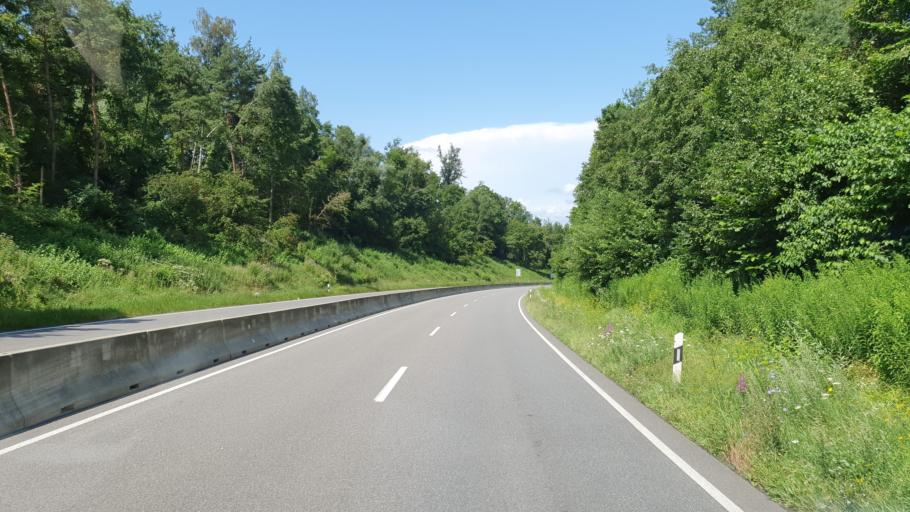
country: DE
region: Baden-Wuerttemberg
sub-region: Tuebingen Region
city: Uhldingen-Muhlhofen
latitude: 47.7210
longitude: 9.2407
